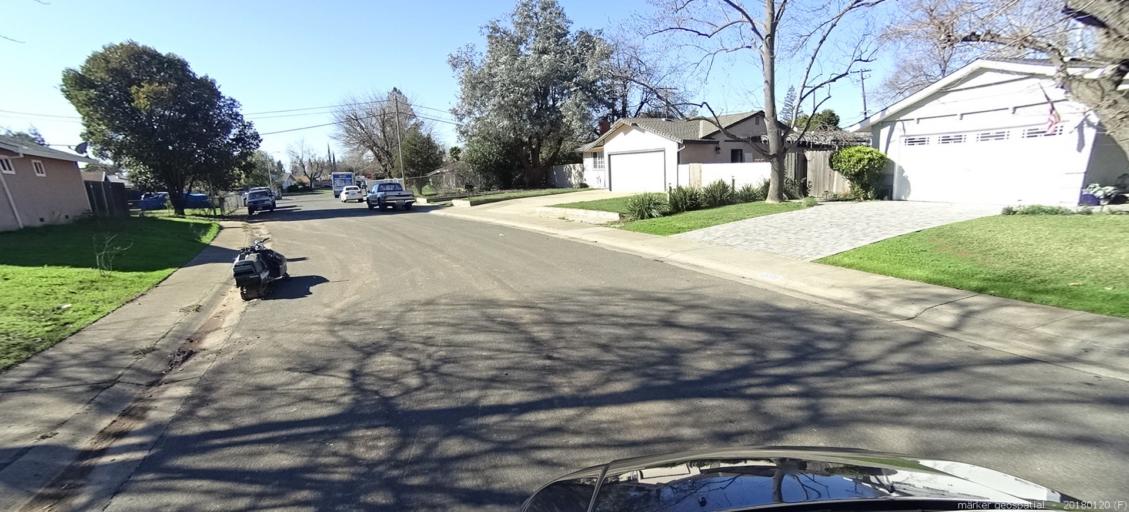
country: US
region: California
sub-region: Sacramento County
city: Rancho Cordova
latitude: 38.5651
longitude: -121.3230
